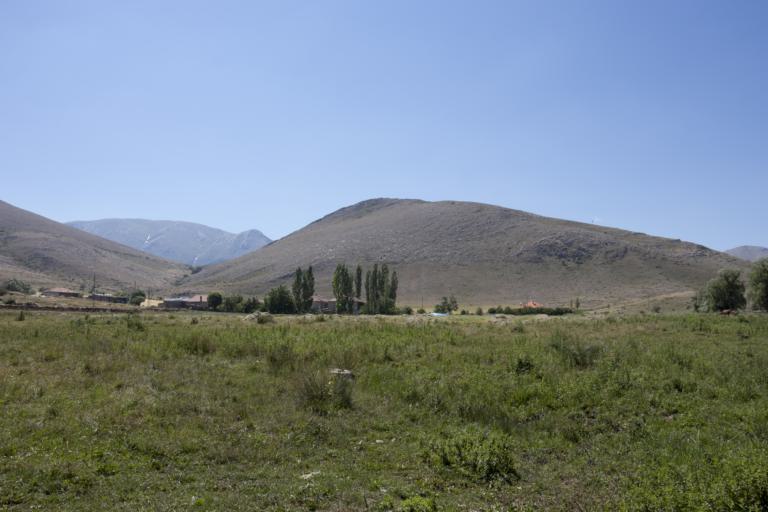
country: TR
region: Kayseri
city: Toklar
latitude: 38.4220
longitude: 36.0969
